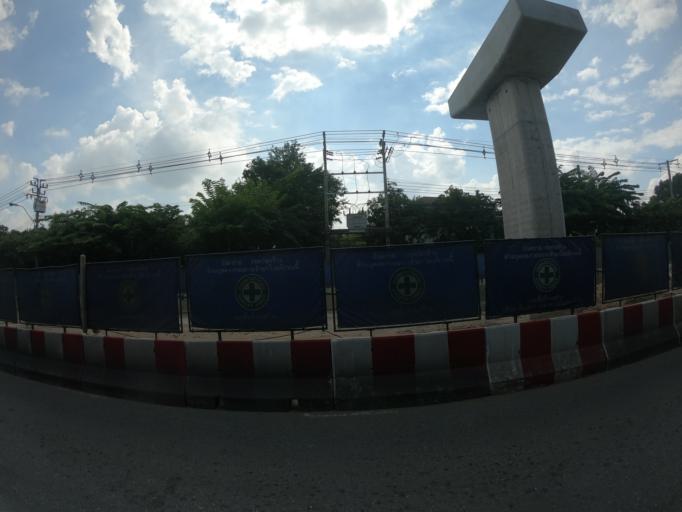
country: TH
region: Bangkok
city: Wang Thonglang
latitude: 13.7919
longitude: 100.5990
